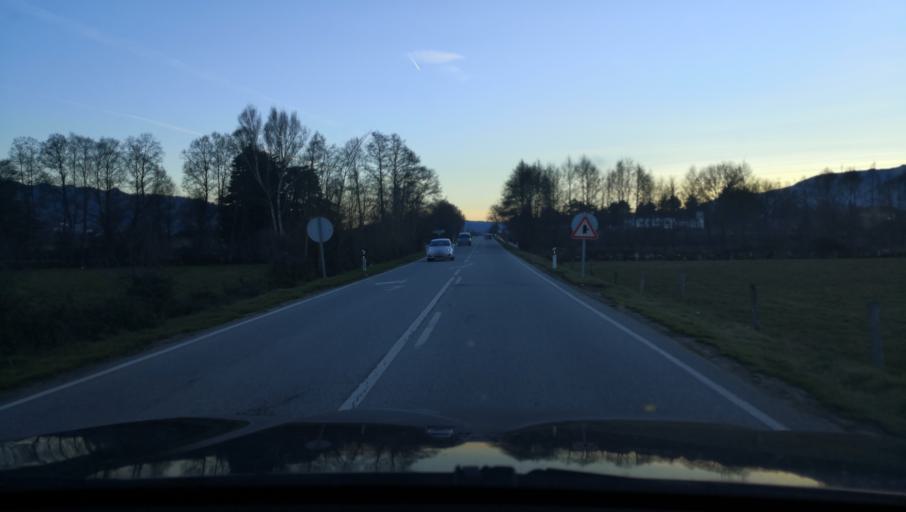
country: PT
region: Vila Real
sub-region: Vila Pouca de Aguiar
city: Vila Pouca de Aguiar
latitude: 41.4408
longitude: -7.6751
